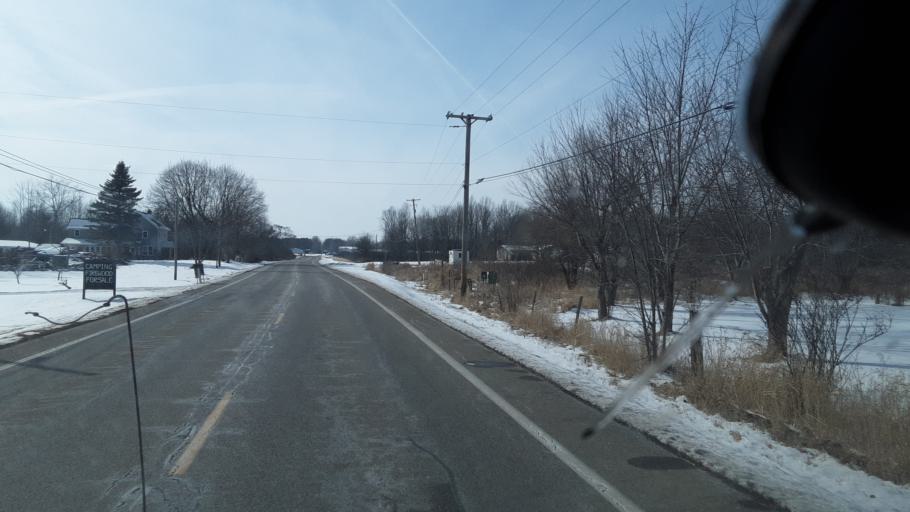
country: US
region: Ohio
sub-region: Mahoning County
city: Craig Beach
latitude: 41.0244
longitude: -80.9777
